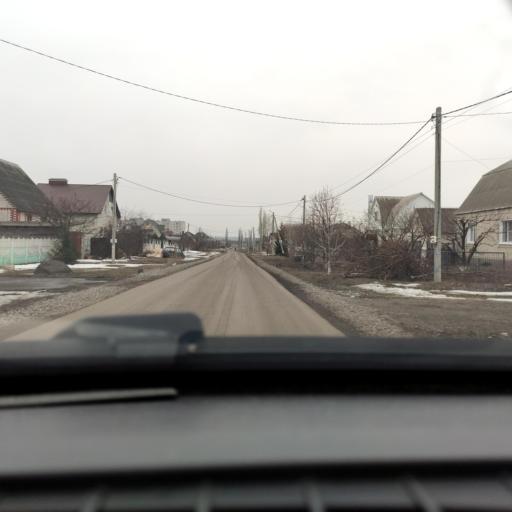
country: RU
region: Voronezj
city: Novaya Usman'
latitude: 51.6582
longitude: 39.4128
